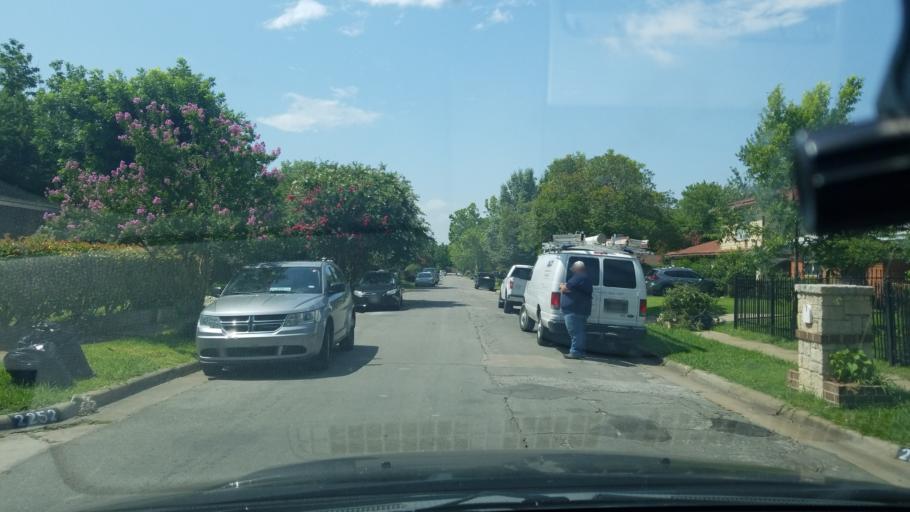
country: US
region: Texas
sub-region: Dallas County
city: Balch Springs
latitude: 32.7526
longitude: -96.6886
